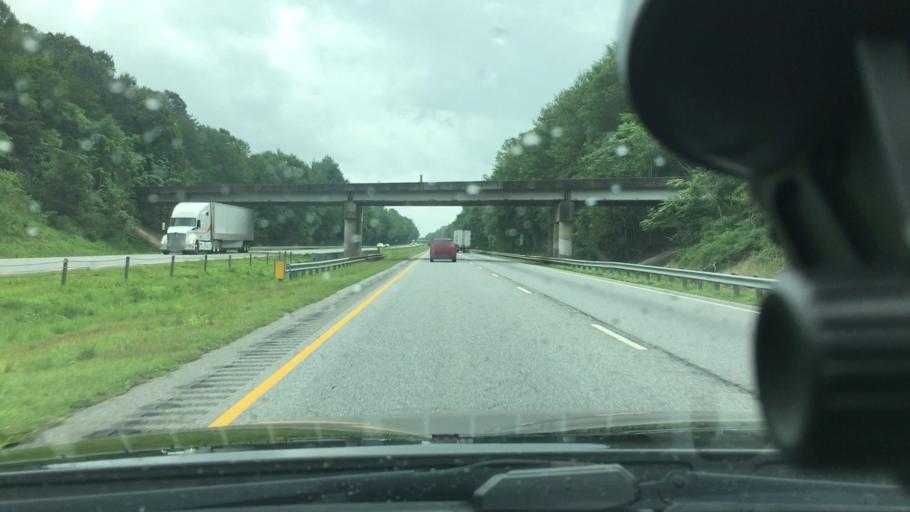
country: US
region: North Carolina
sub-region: Rutherford County
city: Forest City
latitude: 35.3097
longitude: -81.7914
